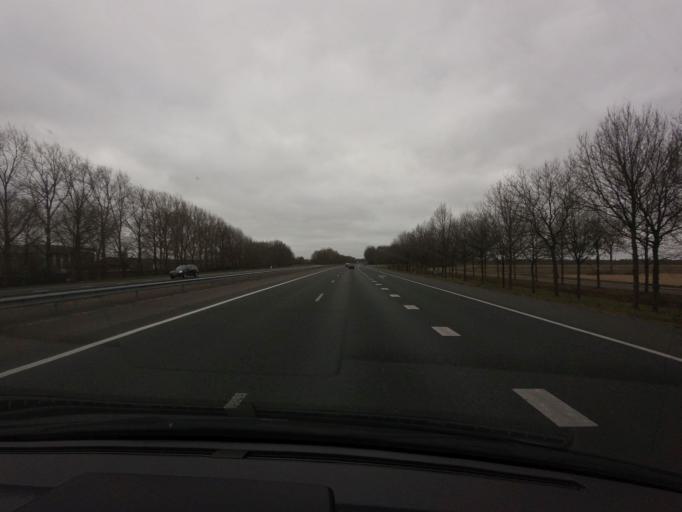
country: NL
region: Groningen
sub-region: Gemeente Hoogezand-Sappemeer
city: Hoogezand
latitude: 53.1690
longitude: 6.7655
